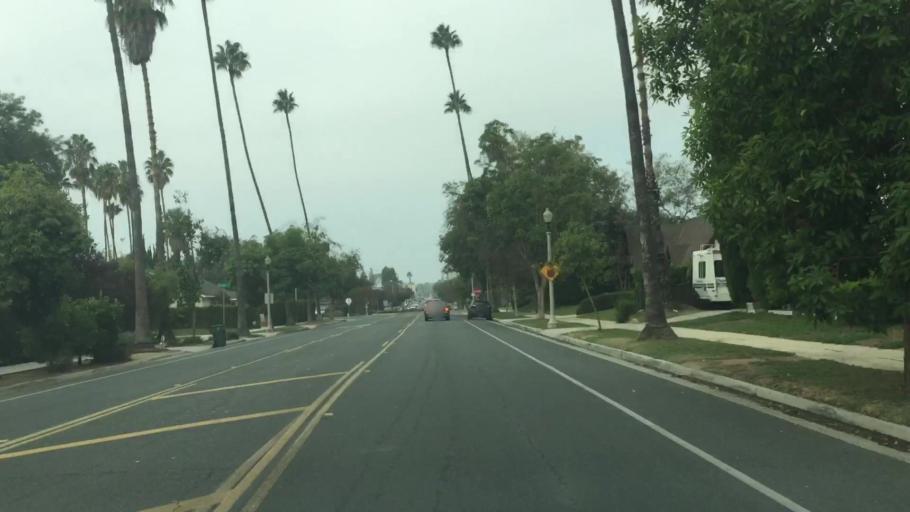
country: US
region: California
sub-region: Los Angeles County
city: South Pasadena
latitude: 34.1276
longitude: -118.1399
